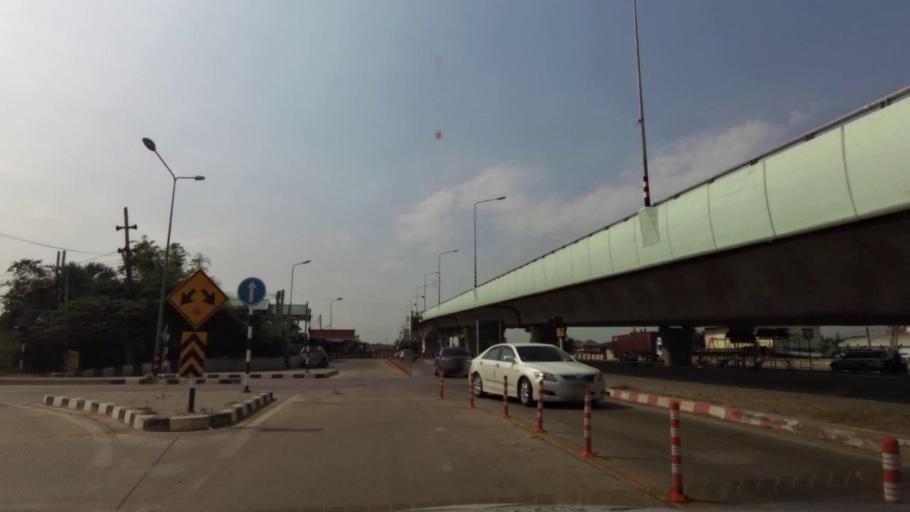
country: TH
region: Phra Nakhon Si Ayutthaya
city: Phra Nakhon Si Ayutthaya
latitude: 14.3296
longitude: 100.5790
